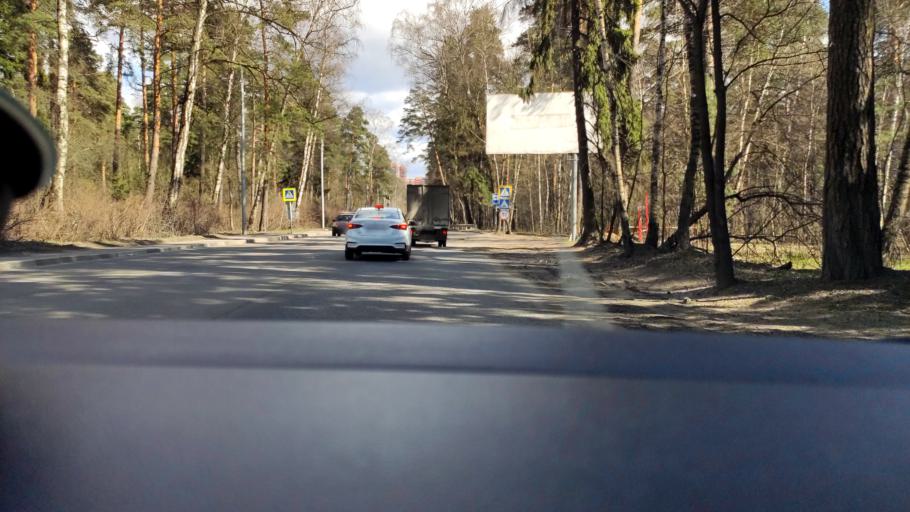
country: RU
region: Moscow
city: Vostochnyy
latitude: 55.8265
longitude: 37.9076
